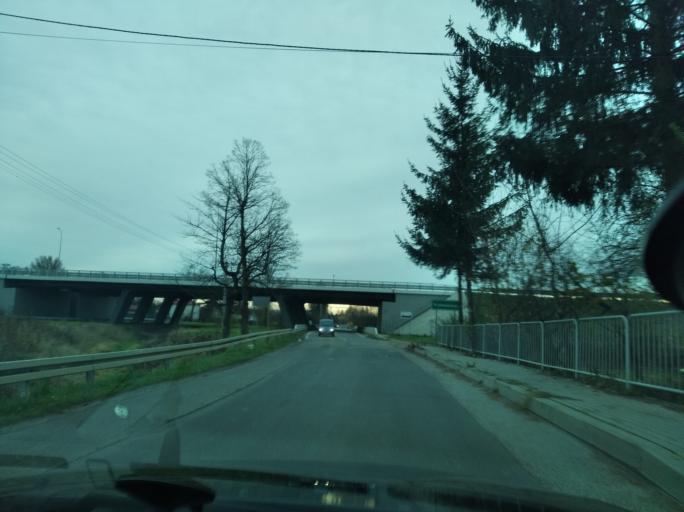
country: PL
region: Subcarpathian Voivodeship
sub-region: Powiat lancucki
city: Czarna
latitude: 50.0915
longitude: 22.1842
